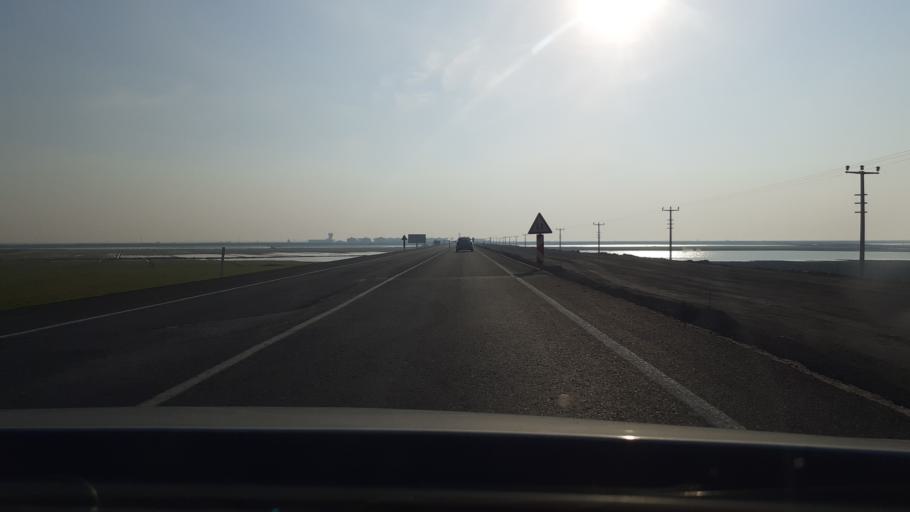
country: TR
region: Hatay
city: Serinyol
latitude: 36.3693
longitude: 36.2573
